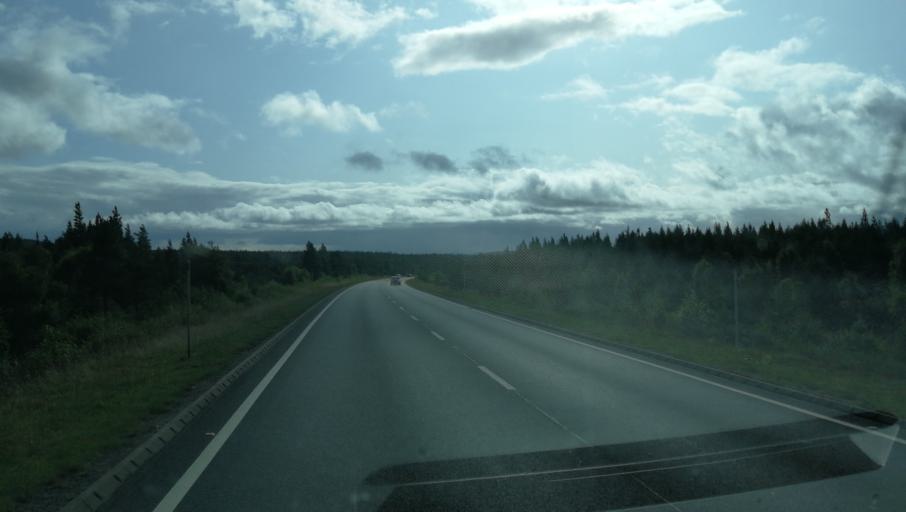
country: GB
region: Scotland
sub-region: Highland
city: Aviemore
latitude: 57.2931
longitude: -3.8602
